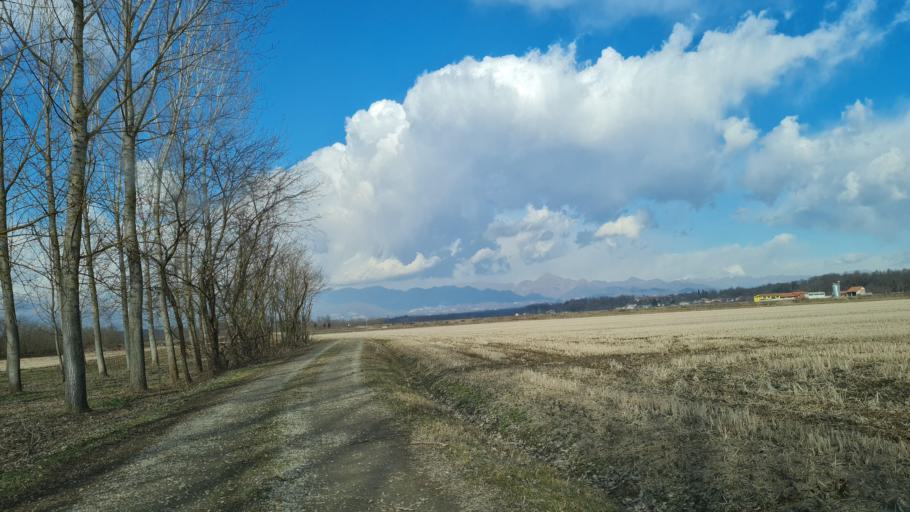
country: IT
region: Piedmont
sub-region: Provincia di Vercelli
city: Buronzo
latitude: 45.4857
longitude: 8.2508
